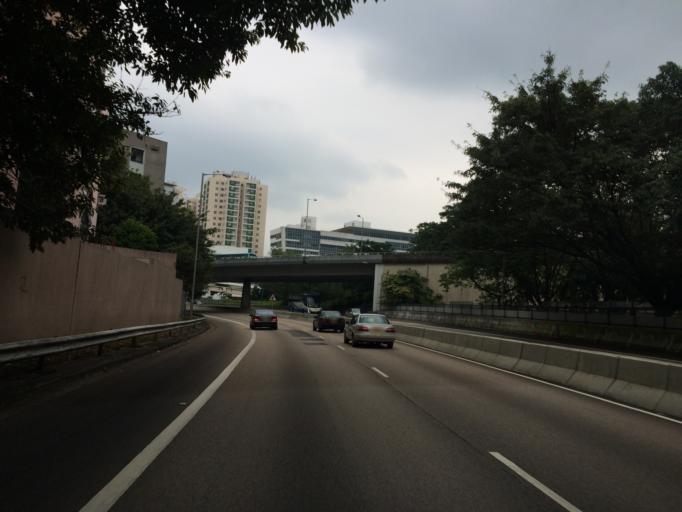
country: HK
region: Sha Tin
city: Sha Tin
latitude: 22.3917
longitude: 114.1975
